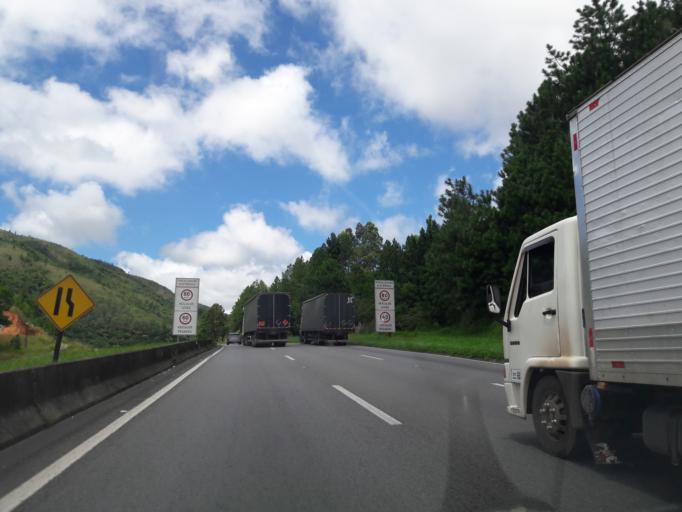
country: BR
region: Parana
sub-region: Campina Grande Do Sul
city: Campina Grande do Sul
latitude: -25.1353
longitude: -48.8573
